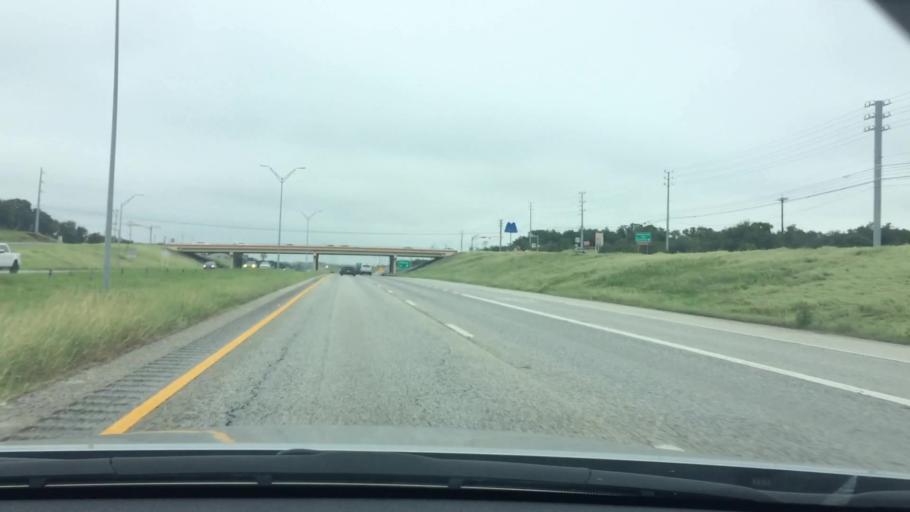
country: US
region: Texas
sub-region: Bexar County
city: Leon Valley
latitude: 29.4651
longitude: -98.6929
